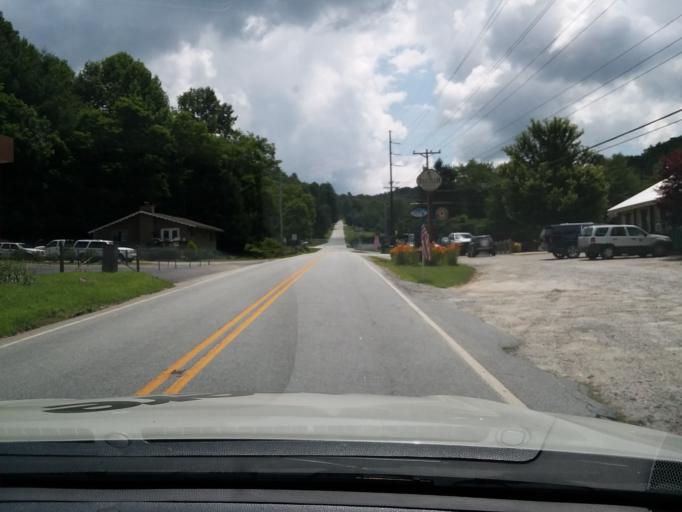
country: US
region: Georgia
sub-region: Rabun County
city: Mountain City
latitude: 35.0223
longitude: -83.3063
